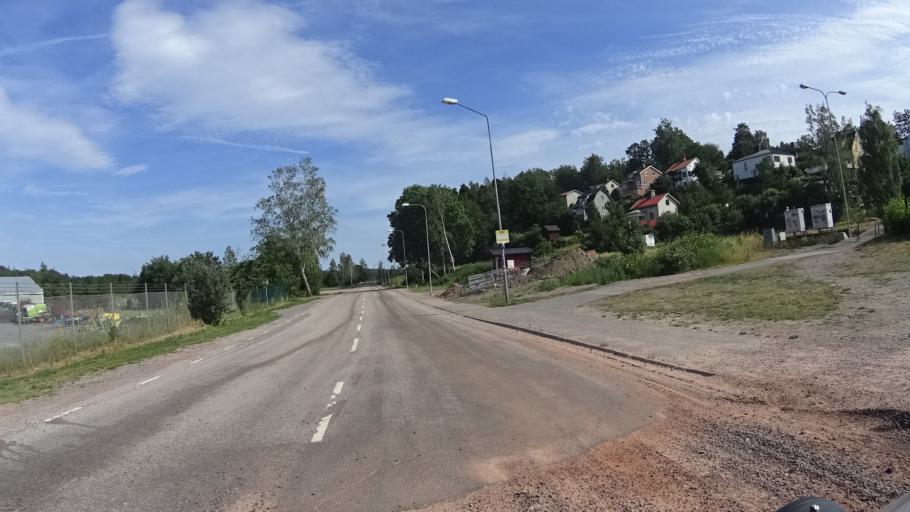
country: SE
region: Kalmar
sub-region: Vasterviks Kommun
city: Gamleby
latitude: 57.8970
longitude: 16.4103
